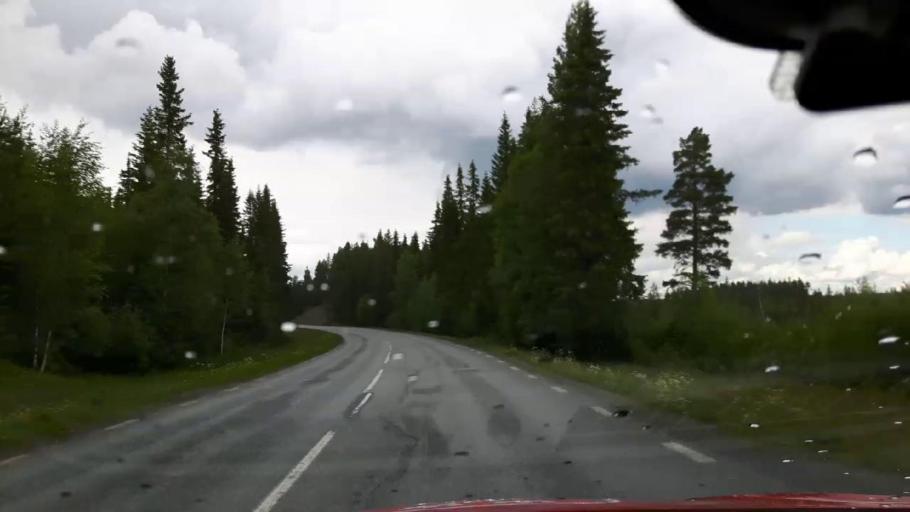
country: SE
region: Jaemtland
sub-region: Krokoms Kommun
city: Krokom
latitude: 63.4138
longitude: 14.2370
